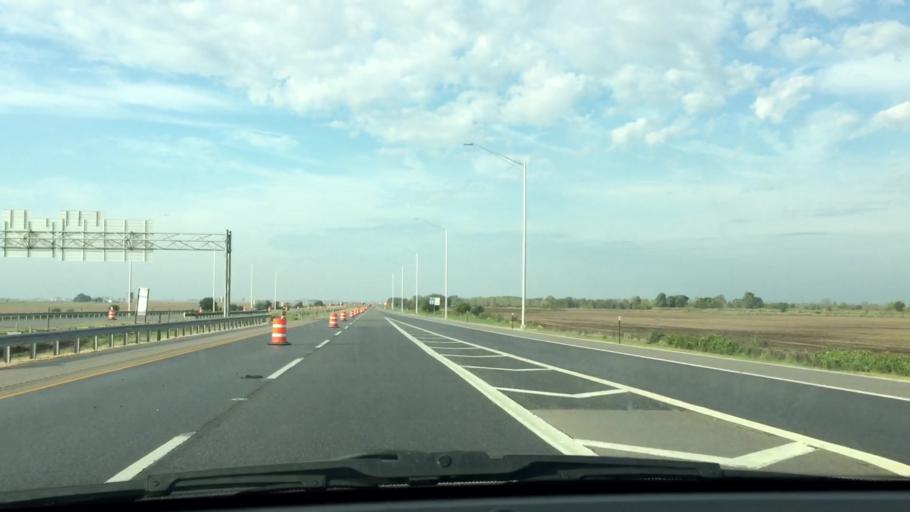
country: US
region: Illinois
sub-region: Ogle County
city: Rochelle
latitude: 41.8989
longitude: -89.0763
